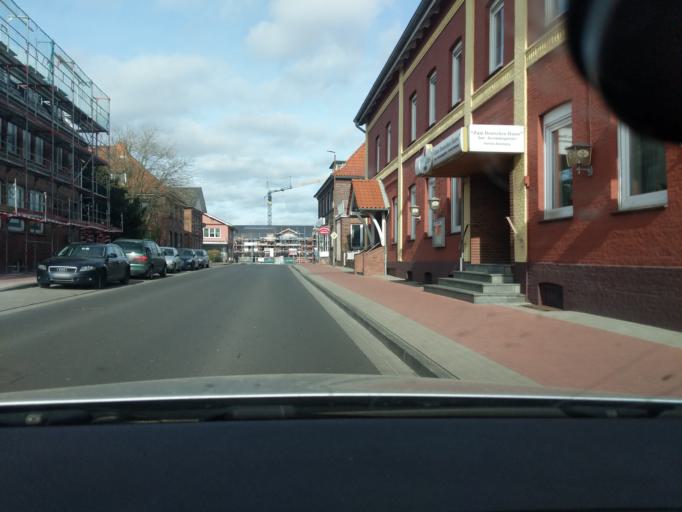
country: DE
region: Lower Saxony
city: Stade
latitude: 53.6528
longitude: 9.4825
